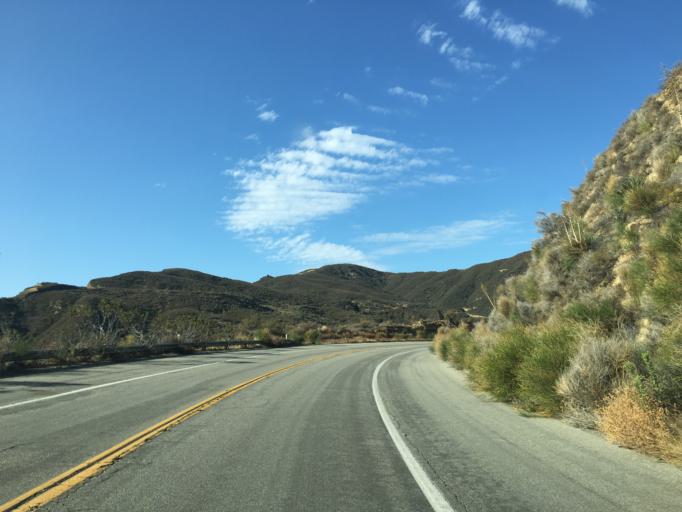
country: US
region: California
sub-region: Los Angeles County
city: Castaic
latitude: 34.5912
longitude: -118.6701
